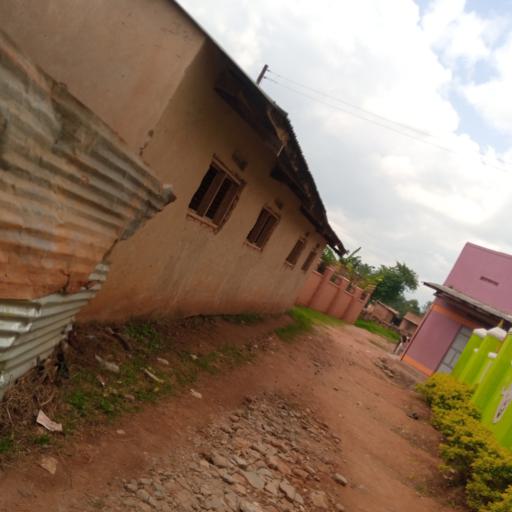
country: UG
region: Eastern Region
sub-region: Mbale District
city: Mbale
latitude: 1.1002
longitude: 34.1767
